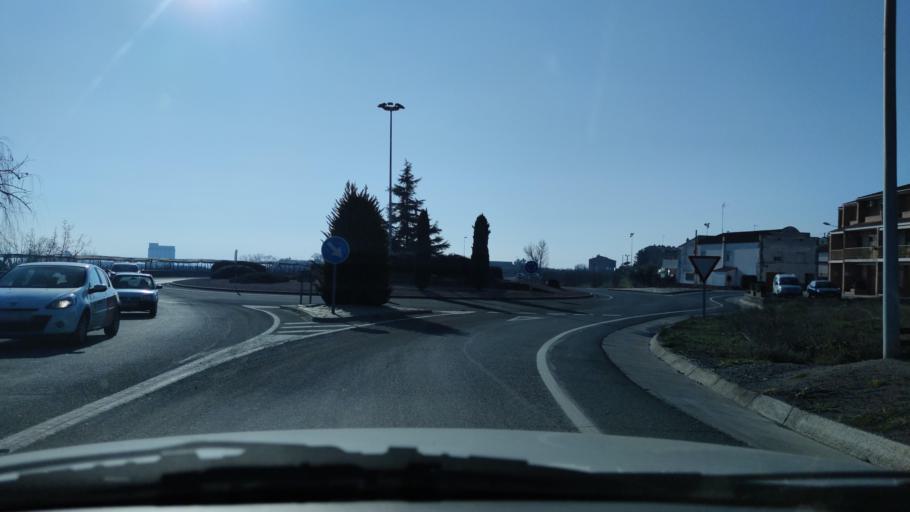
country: ES
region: Catalonia
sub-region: Provincia de Lleida
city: Torrefarrera
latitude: 41.6956
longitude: 0.6362
